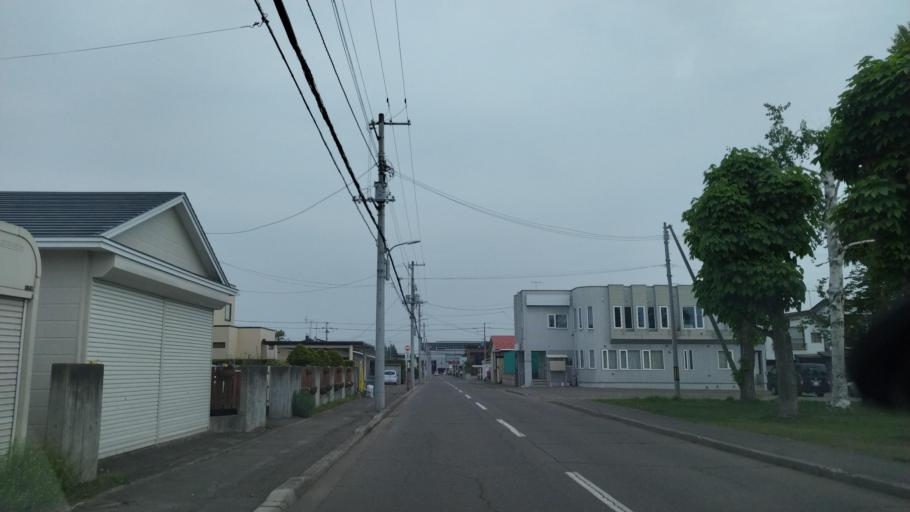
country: JP
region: Hokkaido
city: Obihiro
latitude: 42.9147
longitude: 143.0516
